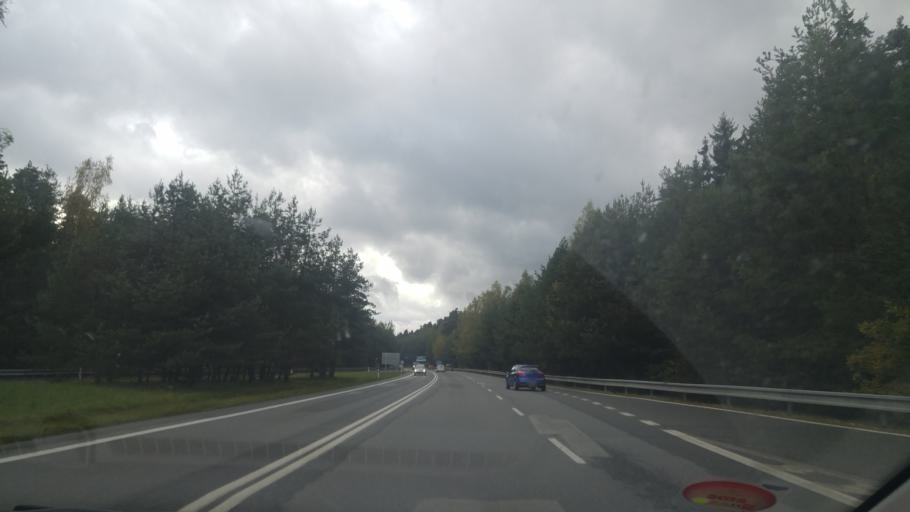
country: CZ
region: Jihocesky
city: Sevetin
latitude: 49.1089
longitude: 14.5675
